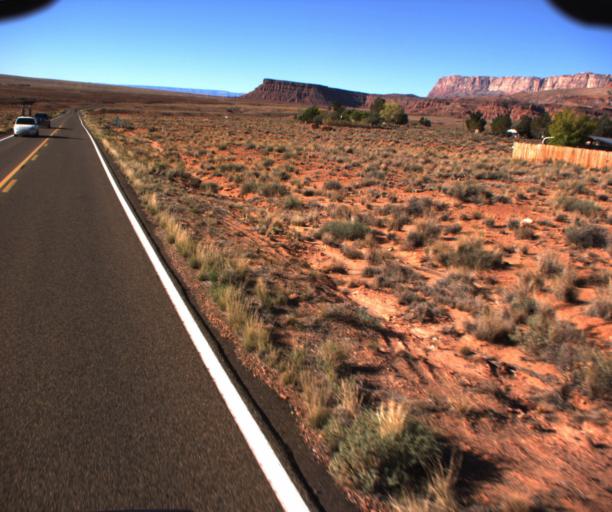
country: US
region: Arizona
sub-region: Coconino County
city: Page
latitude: 36.7870
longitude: -111.6855
